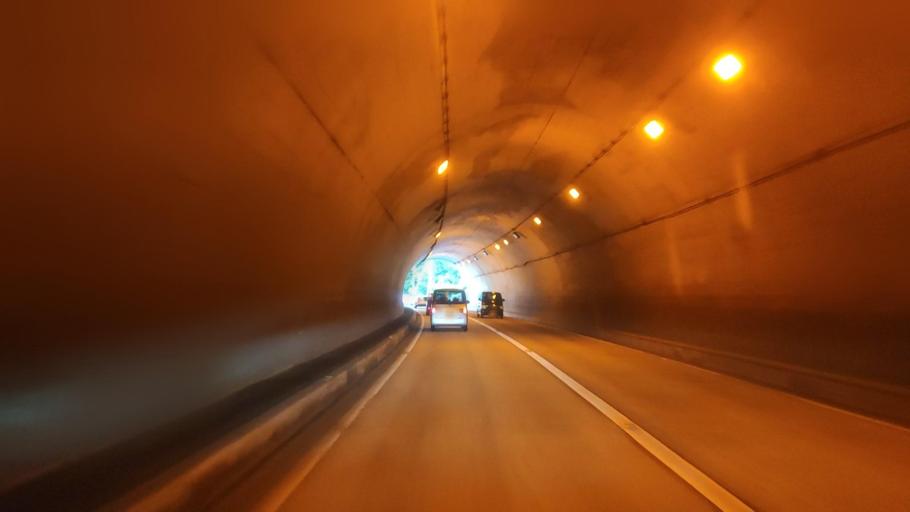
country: JP
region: Wakayama
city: Tanabe
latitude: 33.7287
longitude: 135.4361
